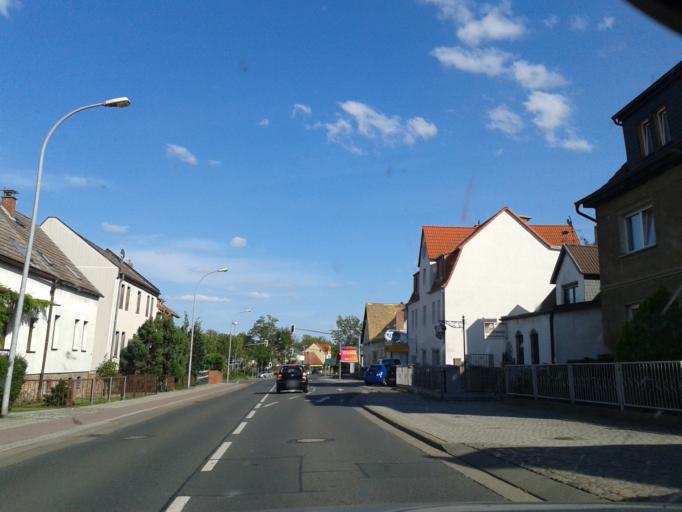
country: DE
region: Saxony-Anhalt
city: Lieskau
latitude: 51.5119
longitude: 11.8780
